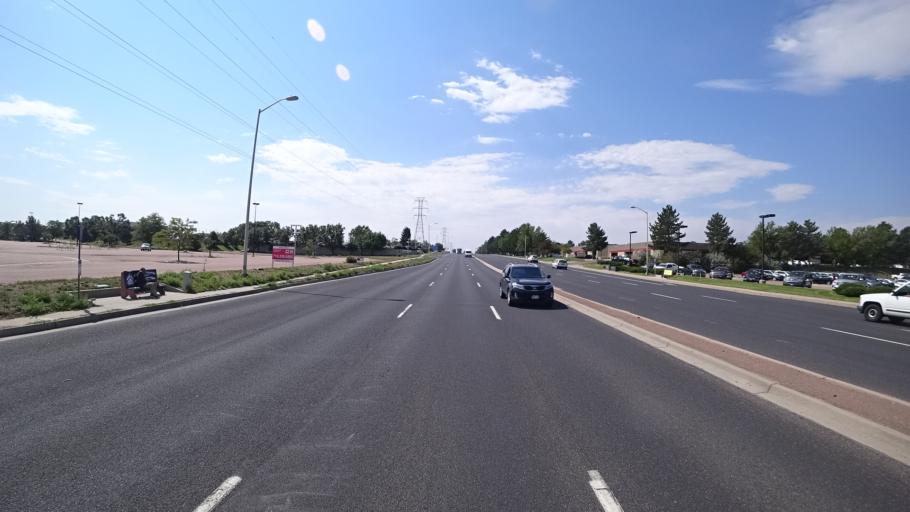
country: US
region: Colorado
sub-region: El Paso County
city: Stratmoor
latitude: 38.8193
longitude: -104.7575
